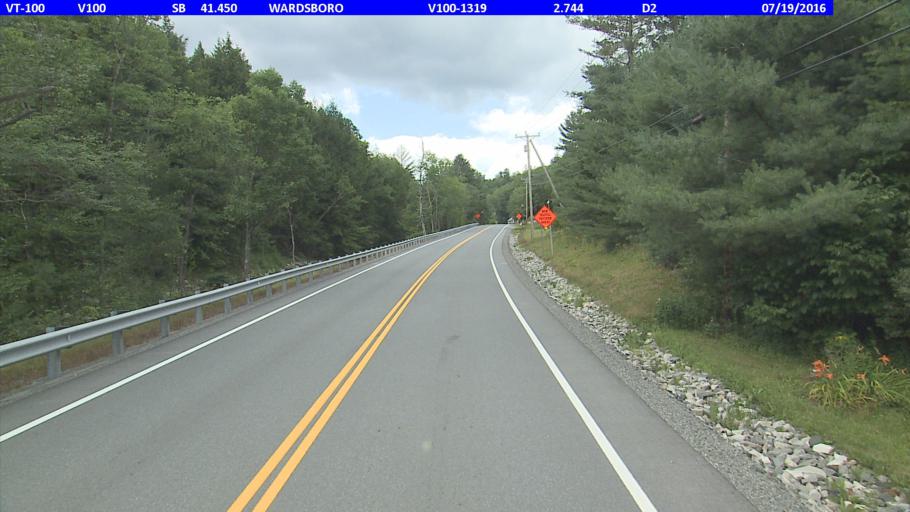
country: US
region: Vermont
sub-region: Windham County
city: Dover
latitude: 43.0371
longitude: -72.8554
